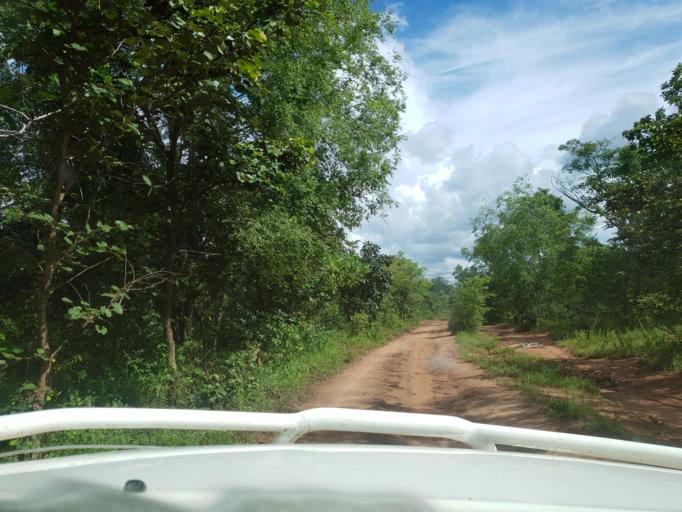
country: CI
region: Savanes
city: Tengrela
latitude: 10.4651
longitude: -6.7977
